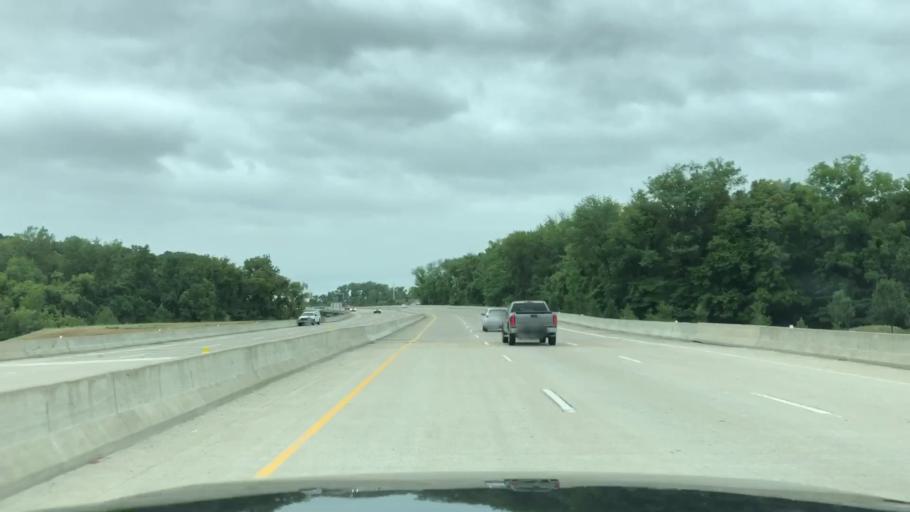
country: US
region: Missouri
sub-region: Saint Louis County
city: Maryland Heights
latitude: 38.6867
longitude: -90.4948
